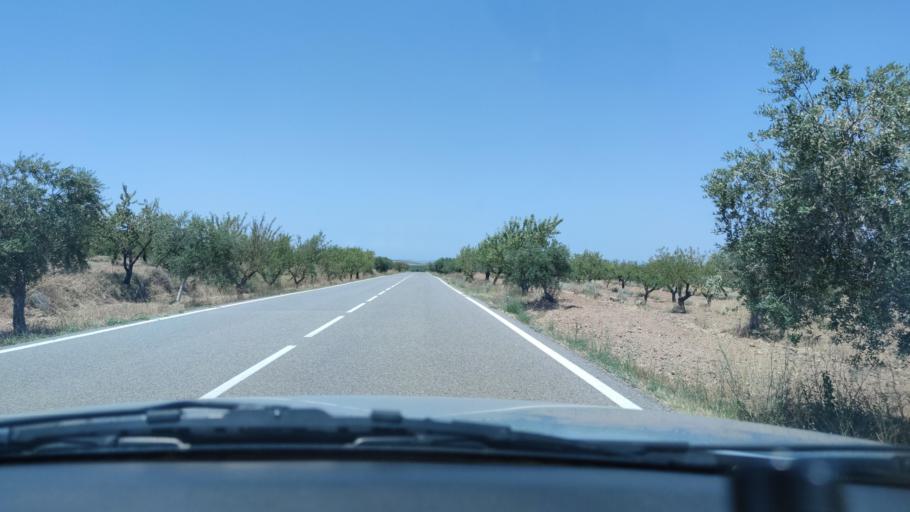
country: ES
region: Catalonia
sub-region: Provincia de Lleida
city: Alcano
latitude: 41.4463
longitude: 0.6401
